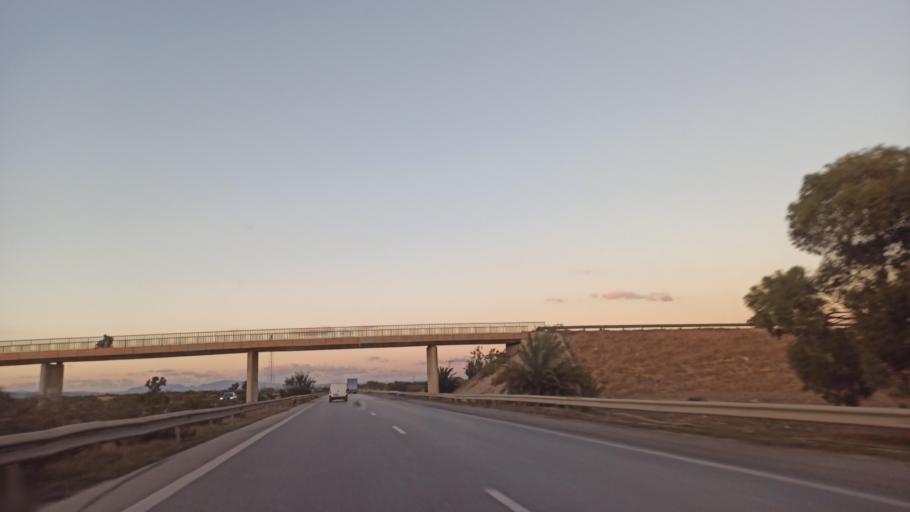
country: TN
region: Nabul
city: Al Hammamat
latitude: 36.2626
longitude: 10.4293
